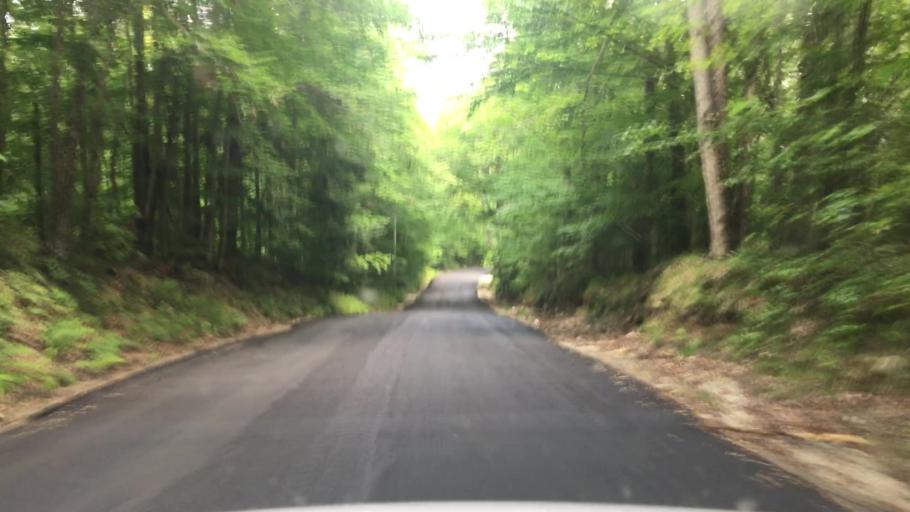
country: US
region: New Hampshire
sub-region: Grafton County
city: Deerfield
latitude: 44.2889
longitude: -71.6573
